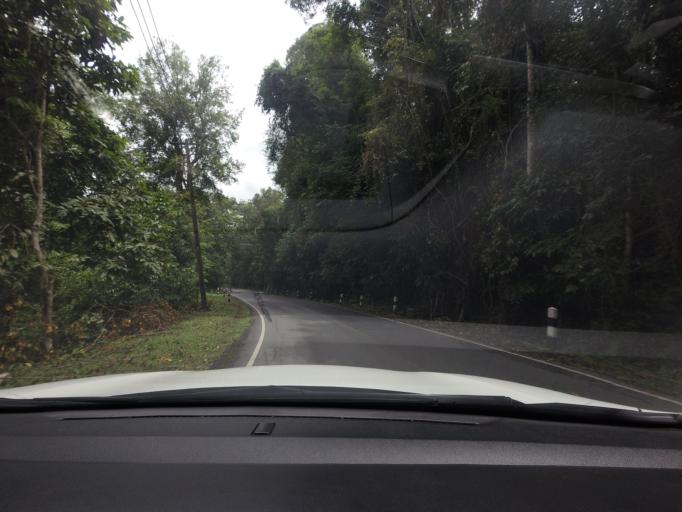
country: TH
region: Nakhon Ratchasima
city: Pak Chong
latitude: 14.4426
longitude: 101.3703
